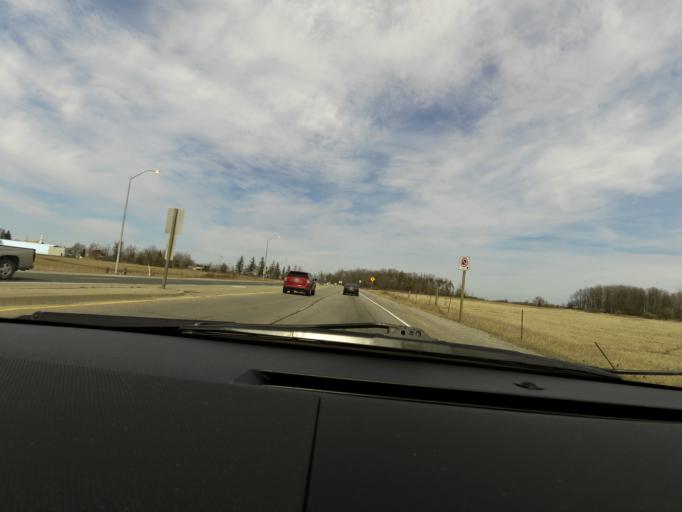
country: CA
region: Ontario
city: Ancaster
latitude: 43.1560
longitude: -79.9117
